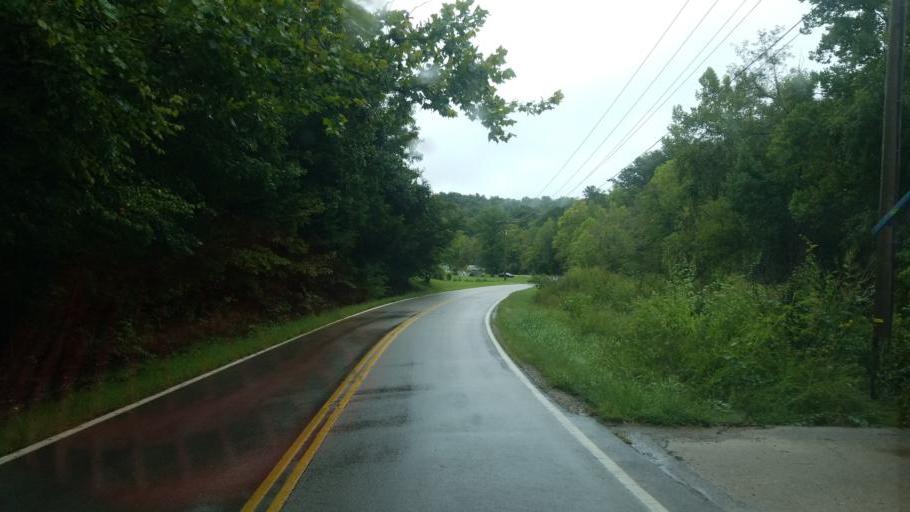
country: US
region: Ohio
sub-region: Adams County
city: West Union
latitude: 38.7676
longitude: -83.5286
